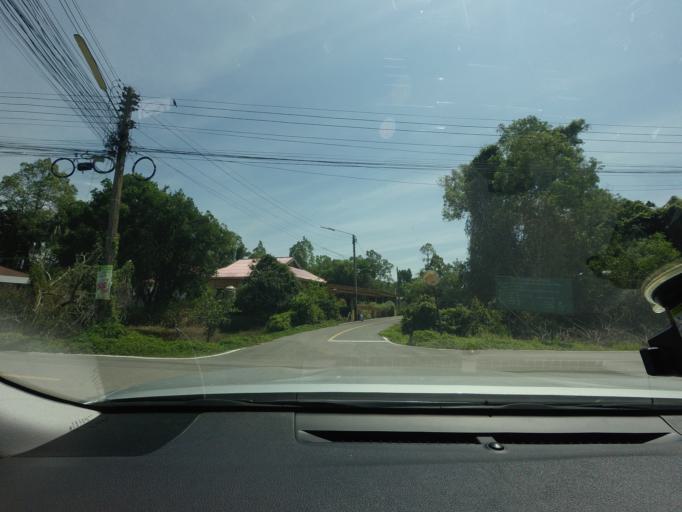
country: TH
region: Narathiwat
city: Narathiwat
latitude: 6.4430
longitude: 101.8101
